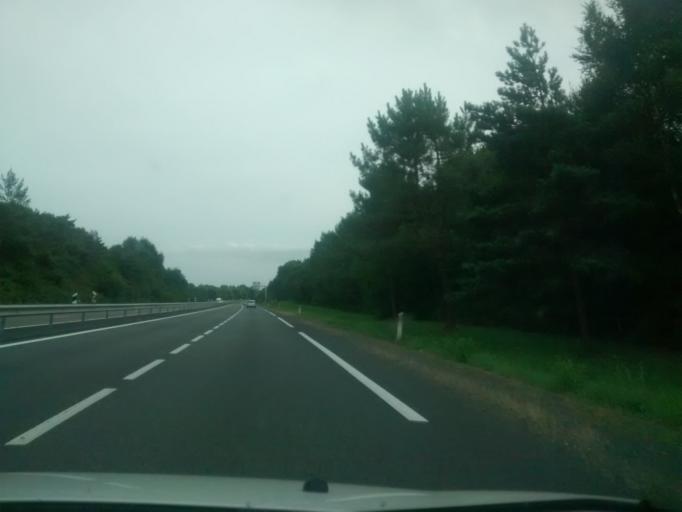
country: FR
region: Brittany
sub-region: Departement d'Ille-et-Vilaine
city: Saint-Pierre-de-Plesguen
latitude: 48.4335
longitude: -1.9194
